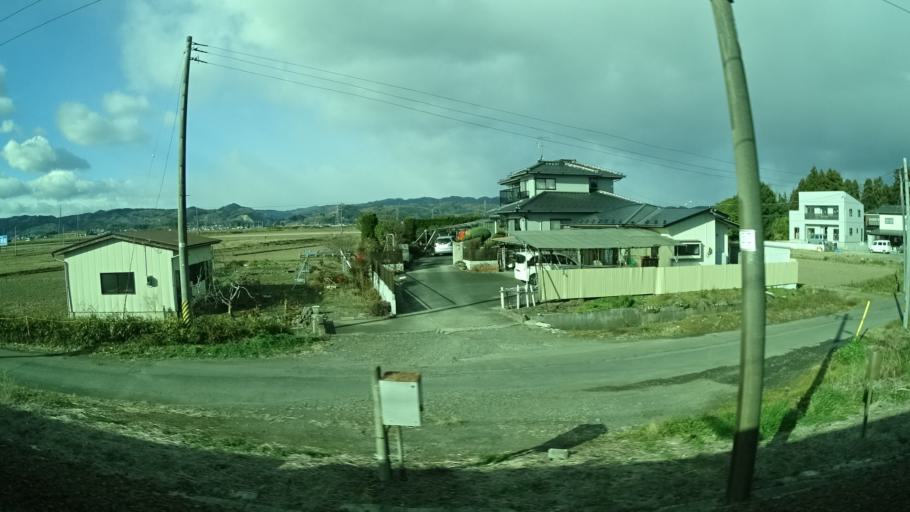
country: JP
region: Miyagi
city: Iwanuma
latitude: 38.1317
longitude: 140.8749
